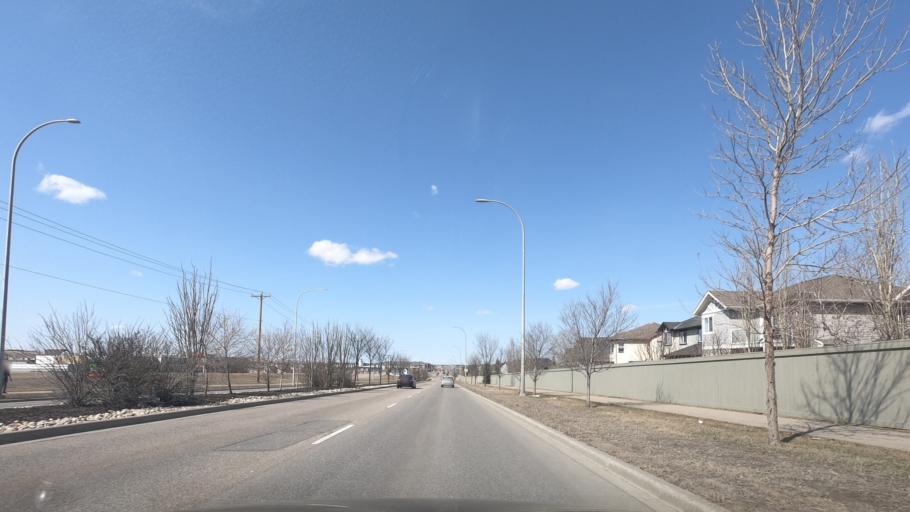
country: CA
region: Alberta
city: Airdrie
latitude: 51.2674
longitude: -114.0252
